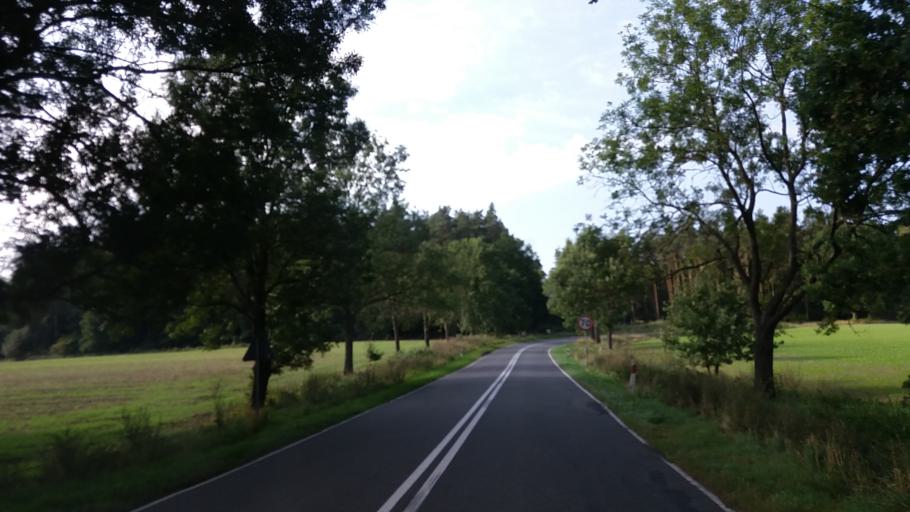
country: PL
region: West Pomeranian Voivodeship
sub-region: Powiat stargardzki
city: Suchan
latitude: 53.2420
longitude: 15.3212
